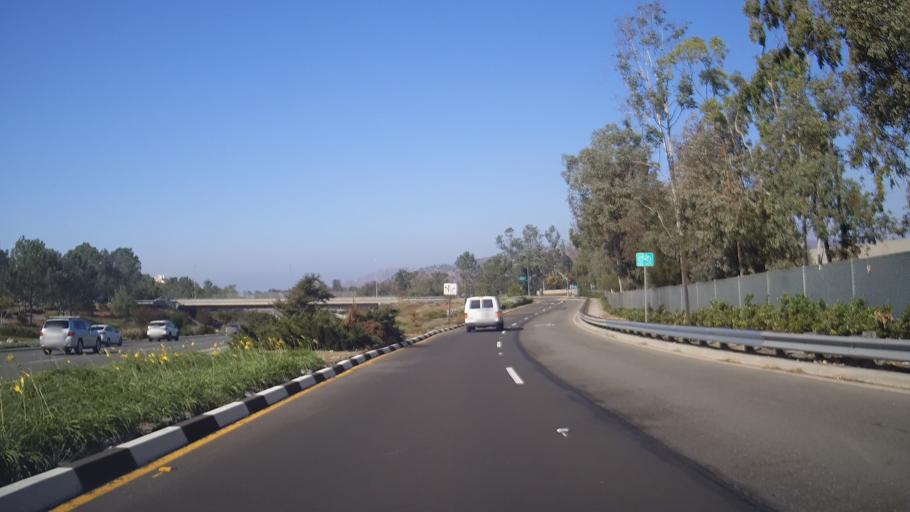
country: US
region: California
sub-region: San Diego County
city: Poway
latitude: 33.0130
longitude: -117.1021
